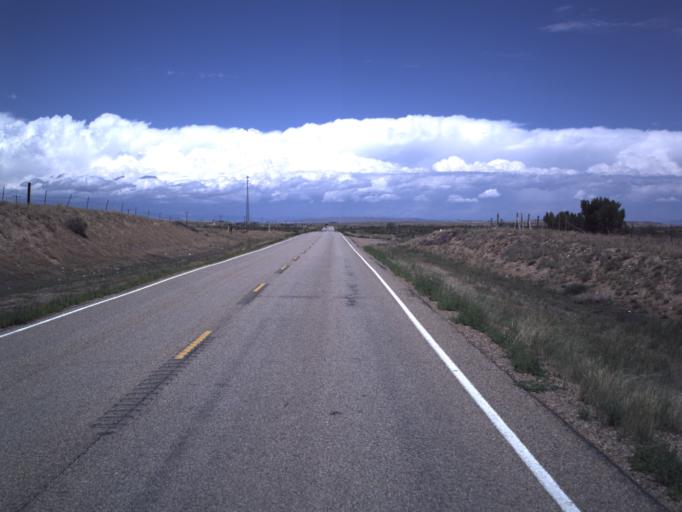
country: US
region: Utah
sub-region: Uintah County
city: Naples
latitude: 40.1050
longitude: -109.6720
